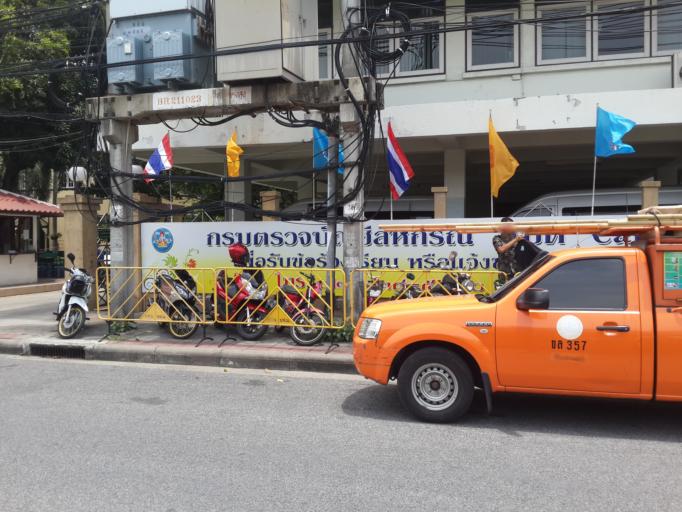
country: TH
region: Bangkok
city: Phra Nakhon
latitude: 13.7710
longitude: 100.5019
